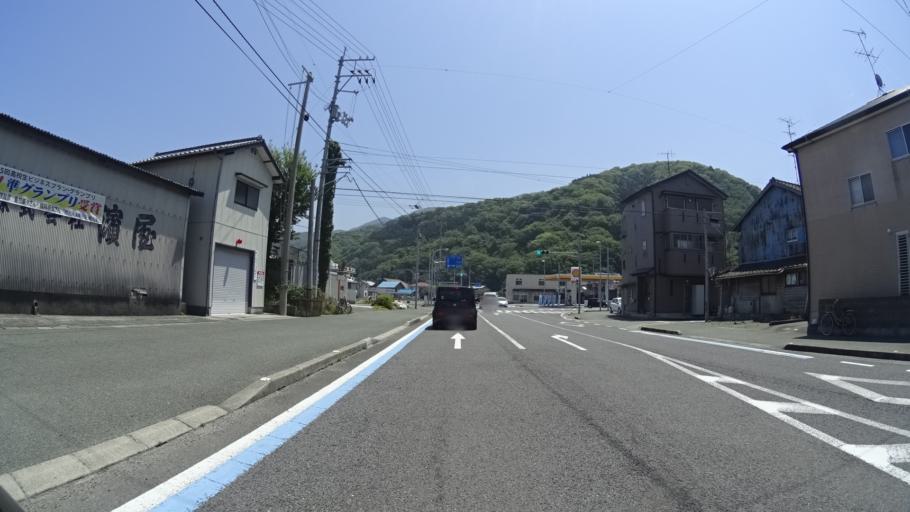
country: JP
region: Ehime
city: Ozu
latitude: 33.6154
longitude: 132.4827
